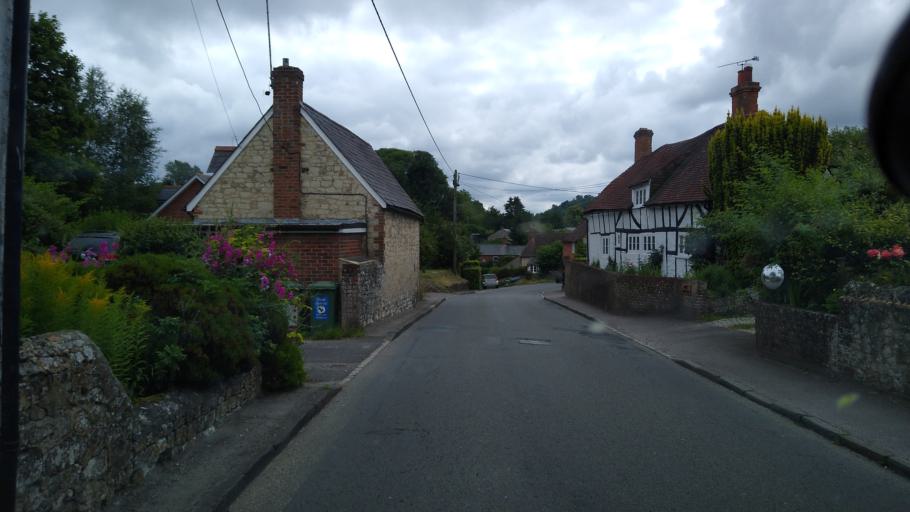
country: GB
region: England
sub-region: Hampshire
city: Alton
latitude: 51.0951
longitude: -0.9389
